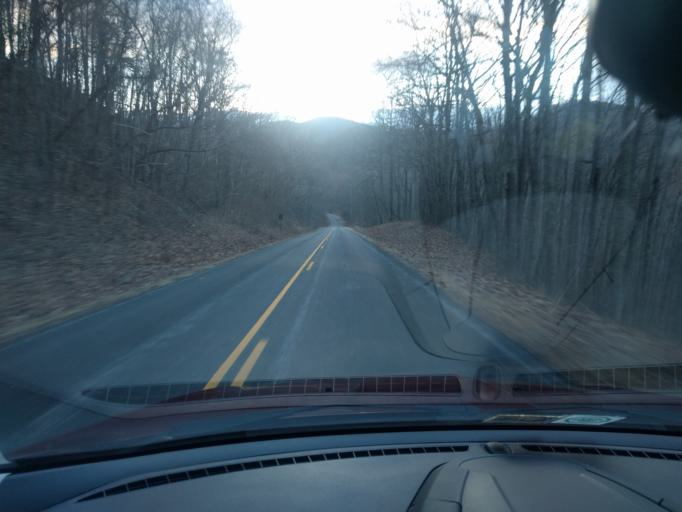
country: US
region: Virginia
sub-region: Botetourt County
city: Buchanan
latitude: 37.4742
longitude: -79.6459
